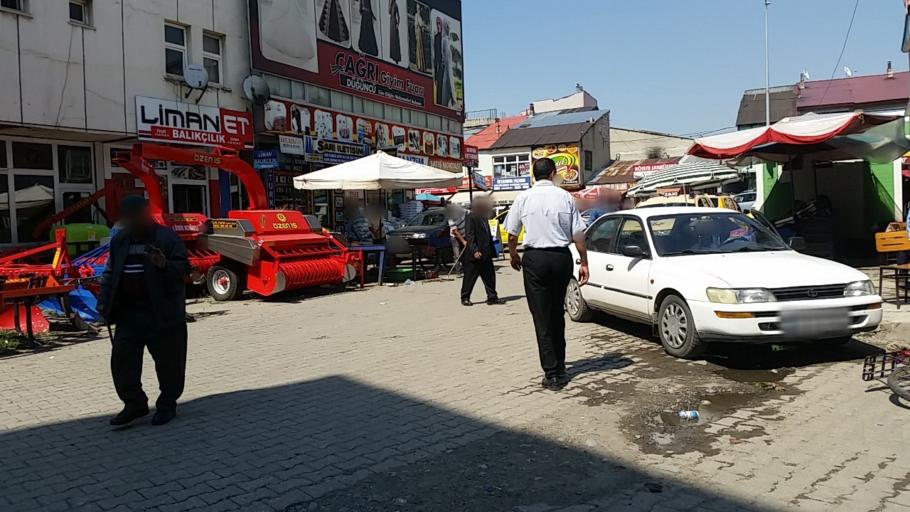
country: TR
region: Agri
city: Agri
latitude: 39.7154
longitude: 43.0523
